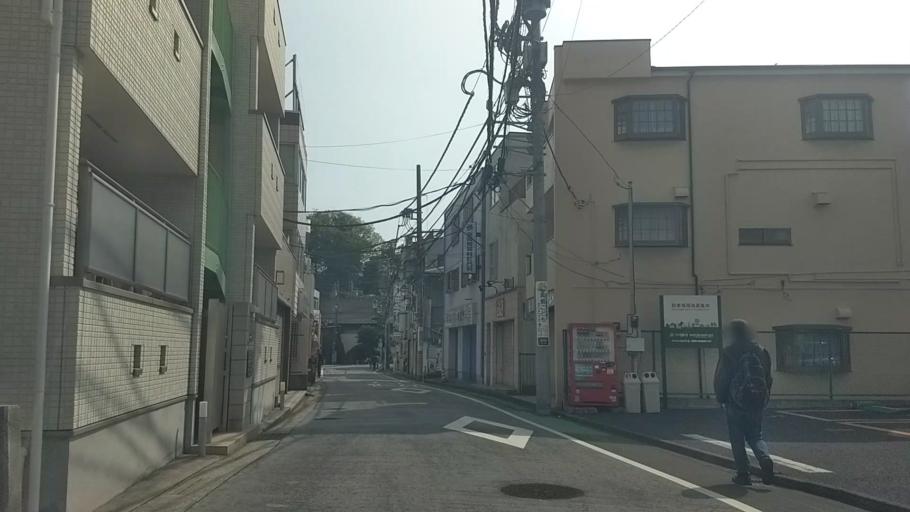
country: JP
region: Kanagawa
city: Yokohama
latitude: 35.3673
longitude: 139.6283
